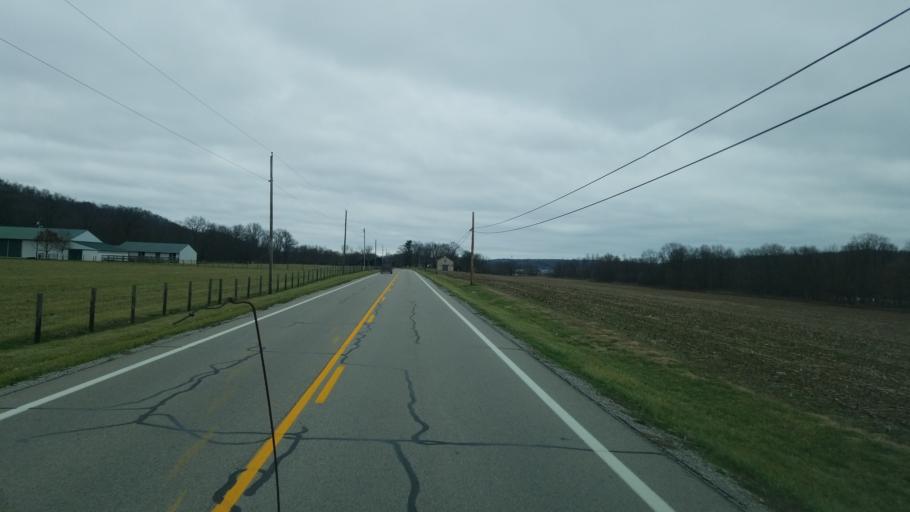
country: US
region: Ohio
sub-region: Clermont County
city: New Richmond
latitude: 38.8060
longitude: -84.2040
